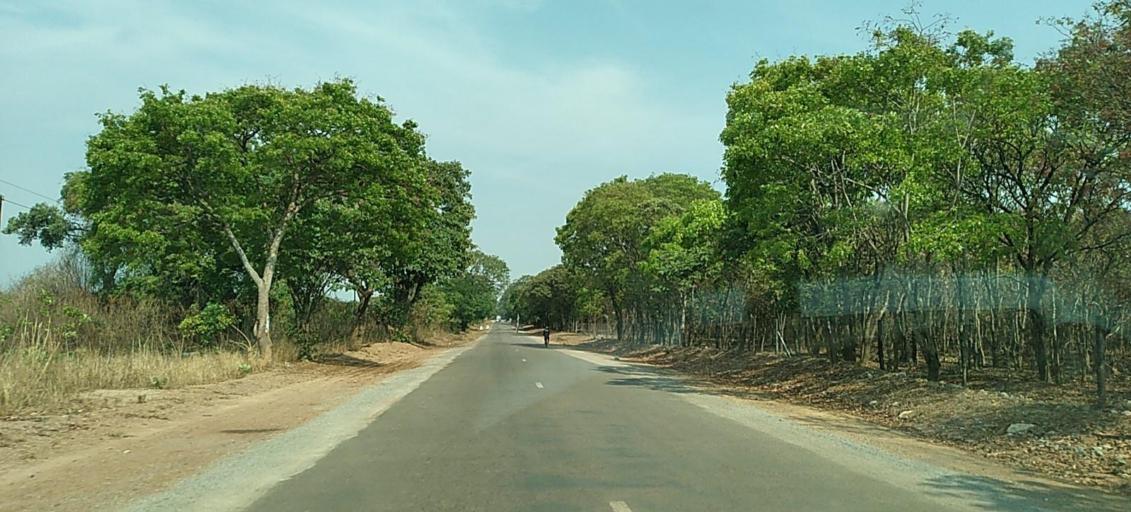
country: ZM
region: Copperbelt
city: Chililabombwe
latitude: -12.3056
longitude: 27.7860
